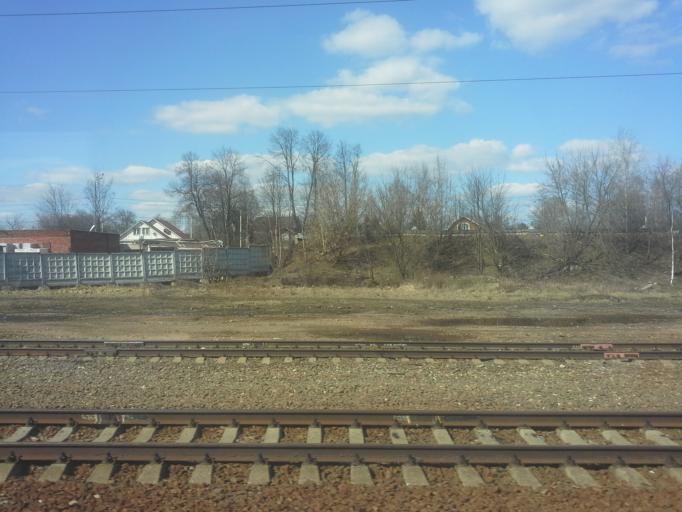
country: RU
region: Moskovskaya
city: Khot'kovo
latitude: 56.2570
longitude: 37.9983
